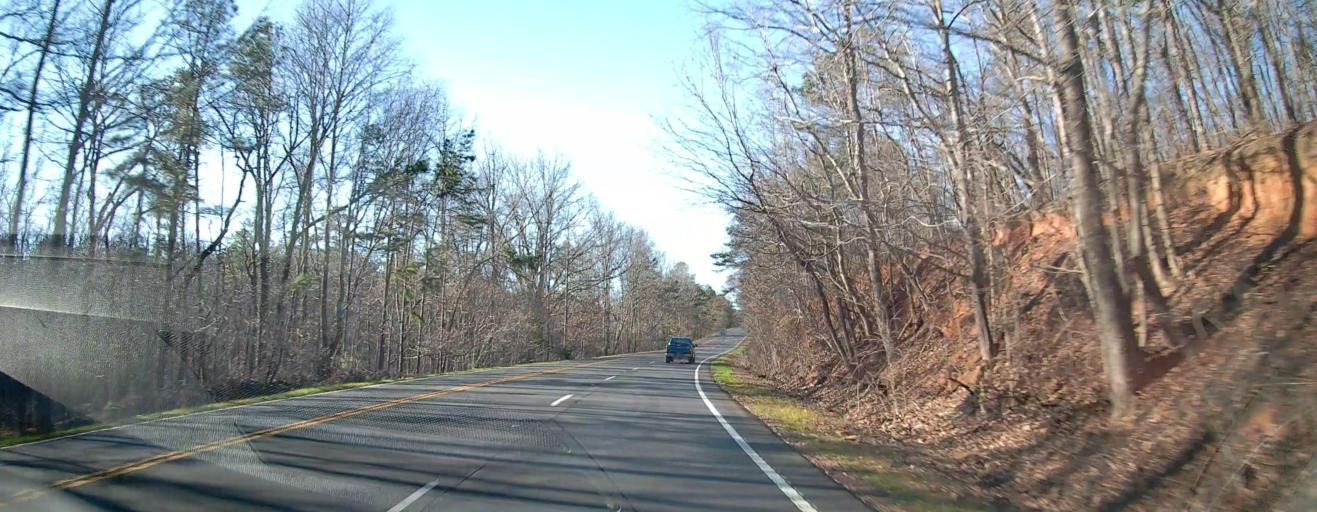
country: US
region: Georgia
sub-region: Talbot County
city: Sardis
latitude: 32.8460
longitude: -84.6961
